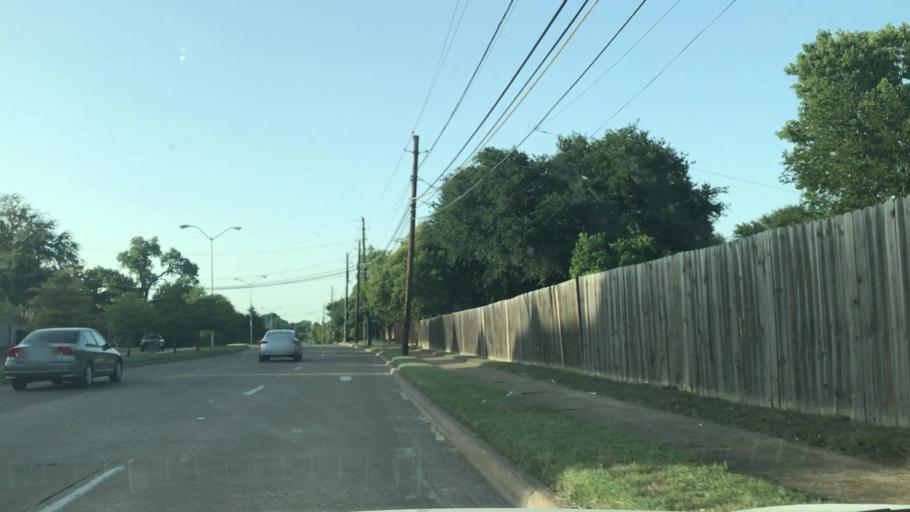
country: US
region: Texas
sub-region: Dallas County
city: Garland
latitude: 32.8663
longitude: -96.7003
